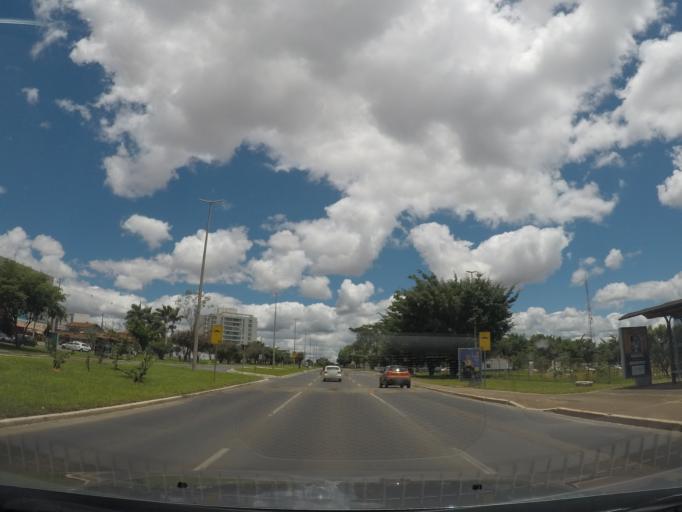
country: BR
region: Federal District
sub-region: Brasilia
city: Brasilia
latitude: -15.8430
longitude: -47.9659
